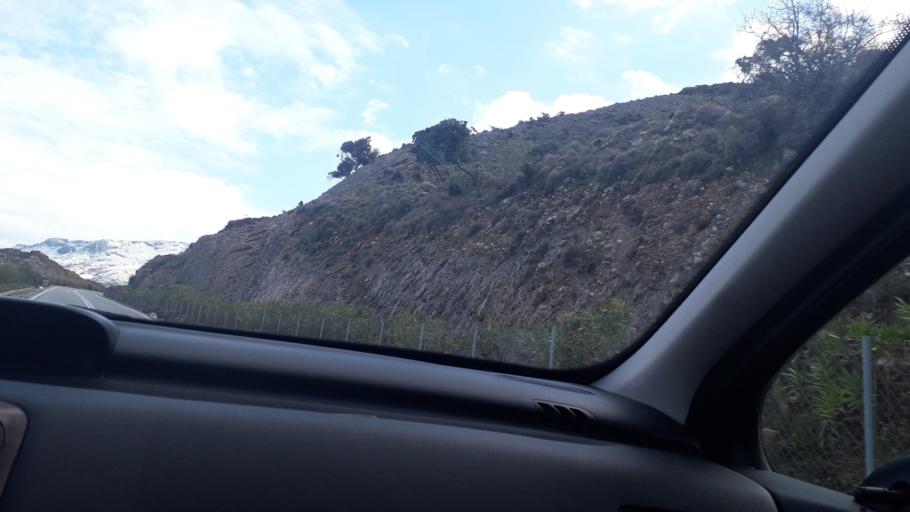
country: GR
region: Crete
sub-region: Nomos Rethymnis
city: Agia Foteini
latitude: 35.2668
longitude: 24.5629
